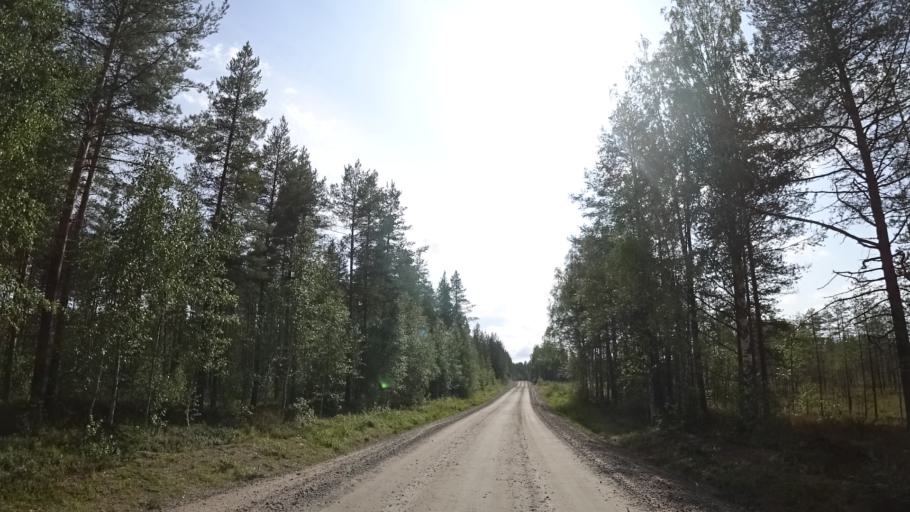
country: FI
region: North Karelia
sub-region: Pielisen Karjala
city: Lieksa
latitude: 63.5447
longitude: 30.0569
